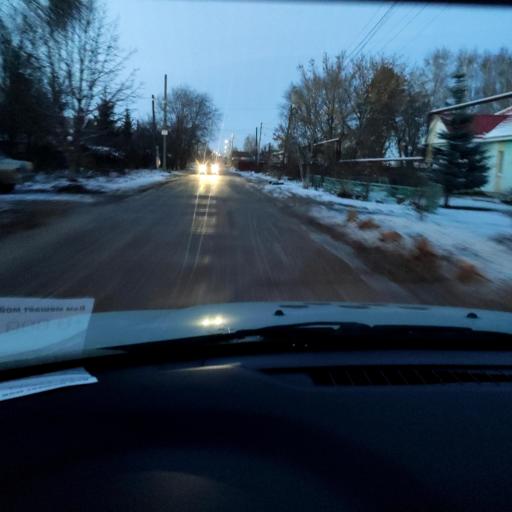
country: RU
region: Samara
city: Tol'yatti
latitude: 53.5640
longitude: 49.3897
